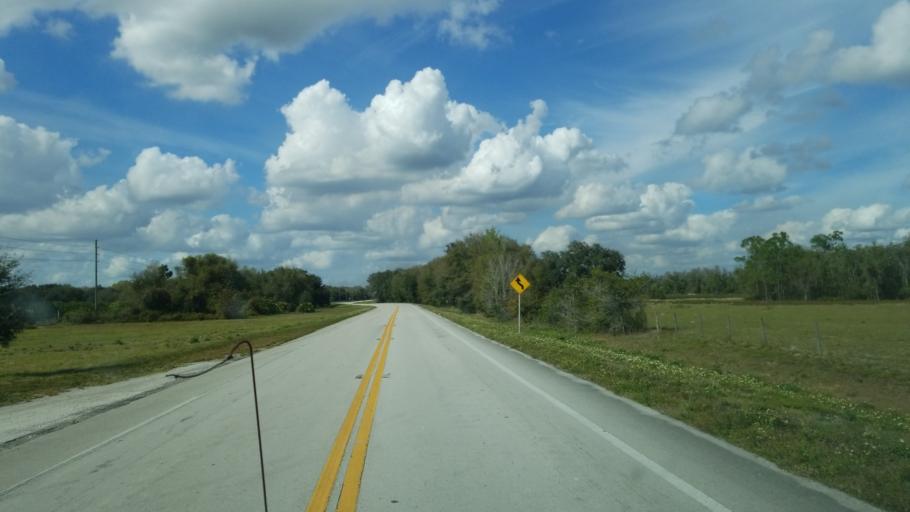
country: US
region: Florida
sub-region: Osceola County
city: Saint Cloud
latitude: 28.0202
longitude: -81.0331
